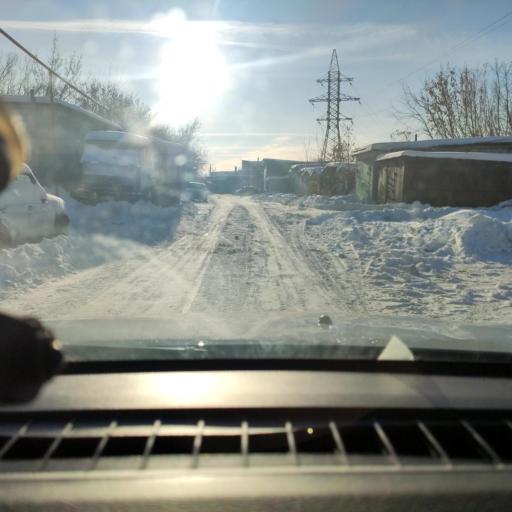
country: RU
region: Samara
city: Petra-Dubrava
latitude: 53.3091
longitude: 50.3036
